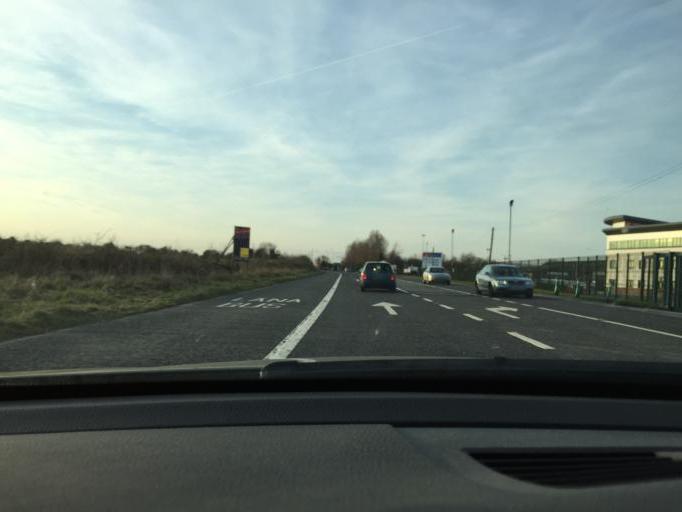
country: IE
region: Leinster
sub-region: An Mhi
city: Dunboyne
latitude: 53.4283
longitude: -6.4591
